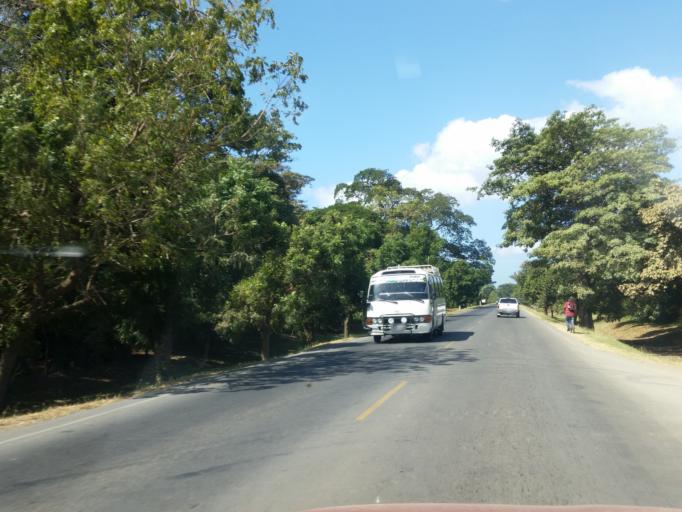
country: NI
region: Granada
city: Nandaime
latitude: 11.7487
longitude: -86.0304
